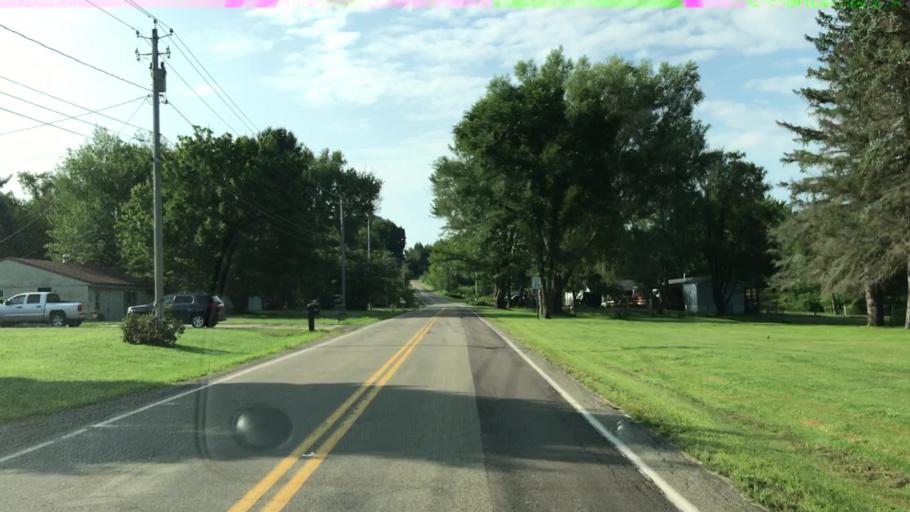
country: US
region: New York
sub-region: Chautauqua County
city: Mayville
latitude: 42.2644
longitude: -79.4710
